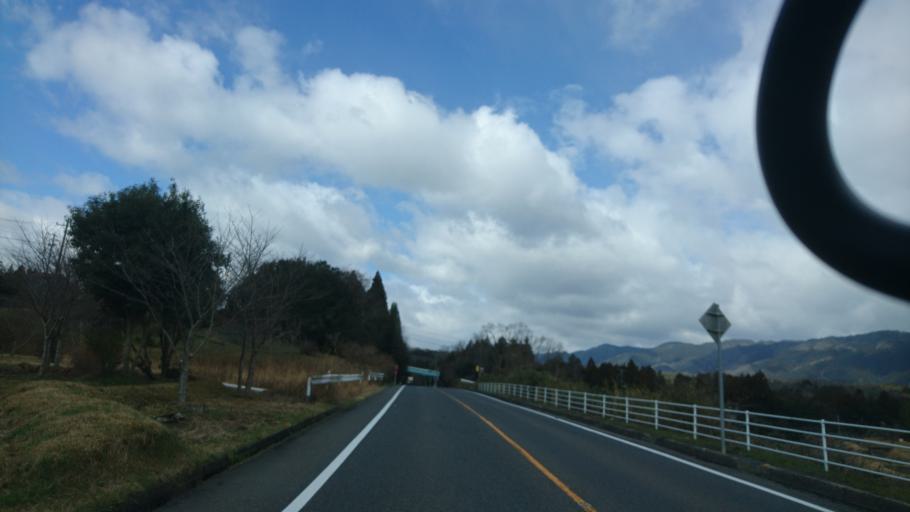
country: JP
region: Mie
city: Ueno-ebisumachi
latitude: 34.7620
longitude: 136.0579
